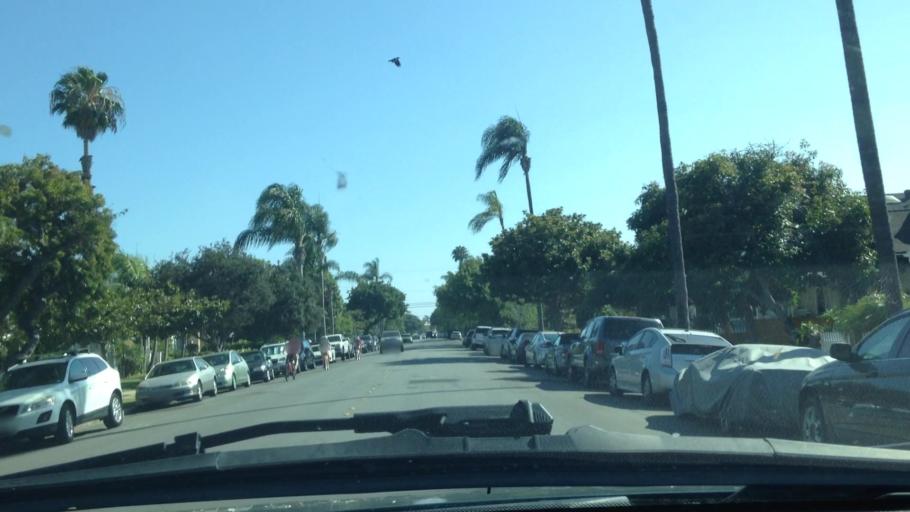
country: US
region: California
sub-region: San Diego County
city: Coronado
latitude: 32.6891
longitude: -117.1751
